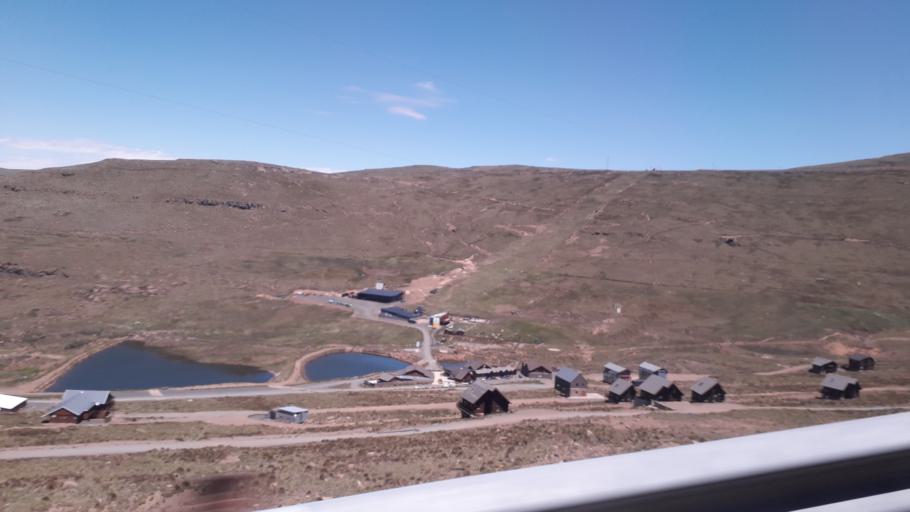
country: ZA
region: Orange Free State
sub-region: Thabo Mofutsanyana District Municipality
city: Phuthaditjhaba
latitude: -28.8241
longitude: 28.7315
